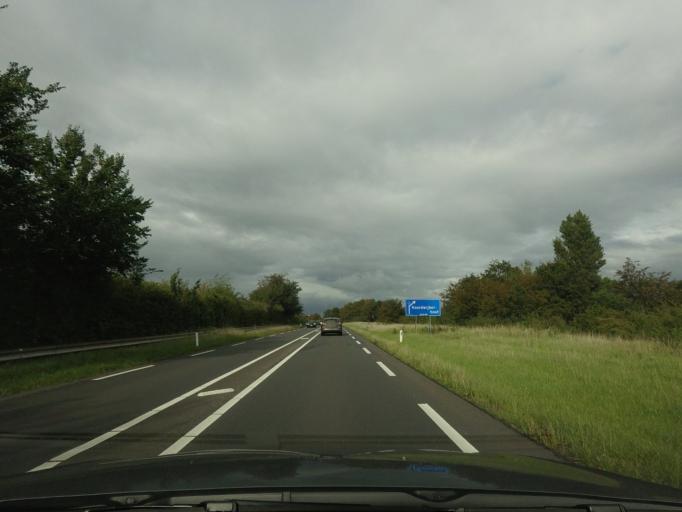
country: NL
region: South Holland
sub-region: Gemeente Noordwijkerhout
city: Noordwijkerhout
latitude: 52.2600
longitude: 4.4952
